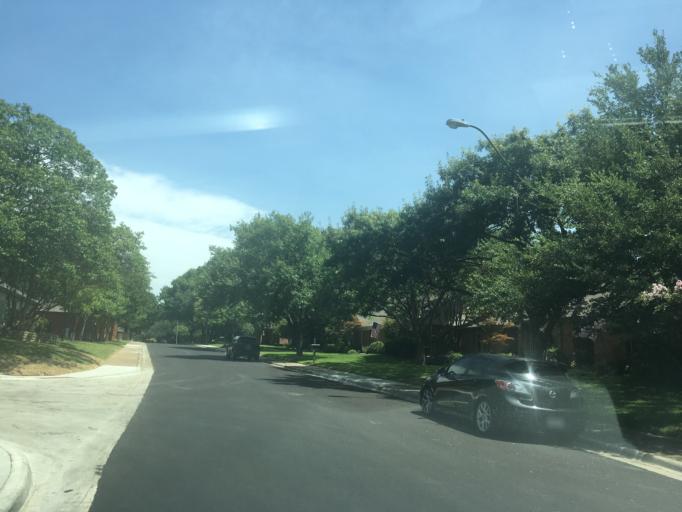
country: US
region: Texas
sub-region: Dallas County
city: Richardson
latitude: 32.8802
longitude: -96.7384
